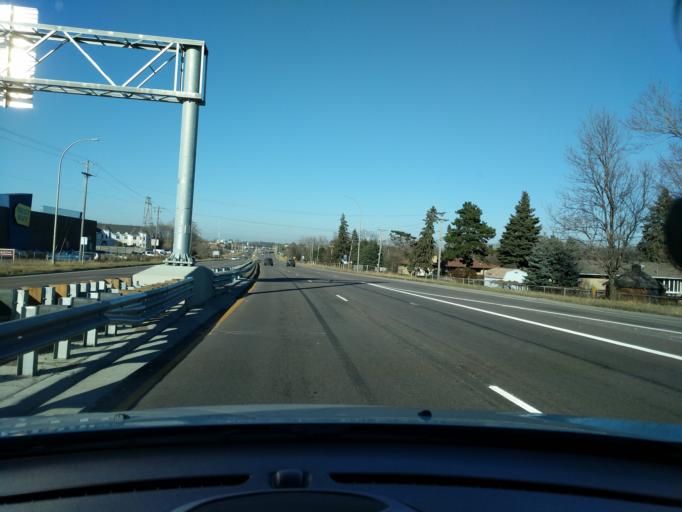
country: US
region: Minnesota
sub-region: Ramsey County
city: Roseville
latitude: 45.0155
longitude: -93.1669
